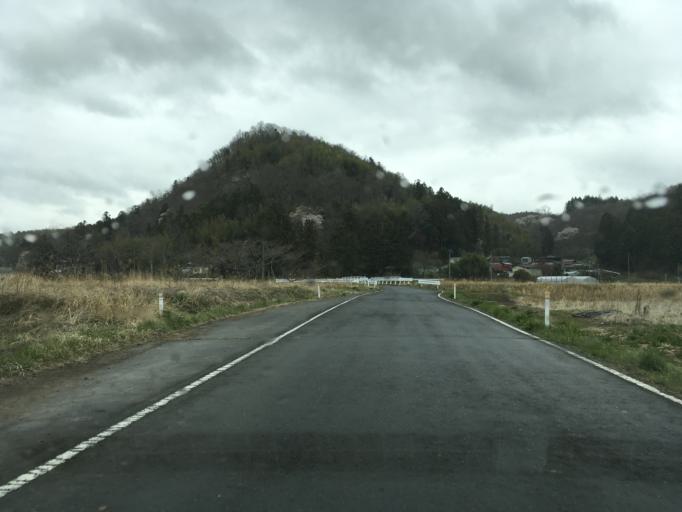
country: JP
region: Iwate
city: Ichinoseki
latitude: 38.7478
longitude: 141.2189
